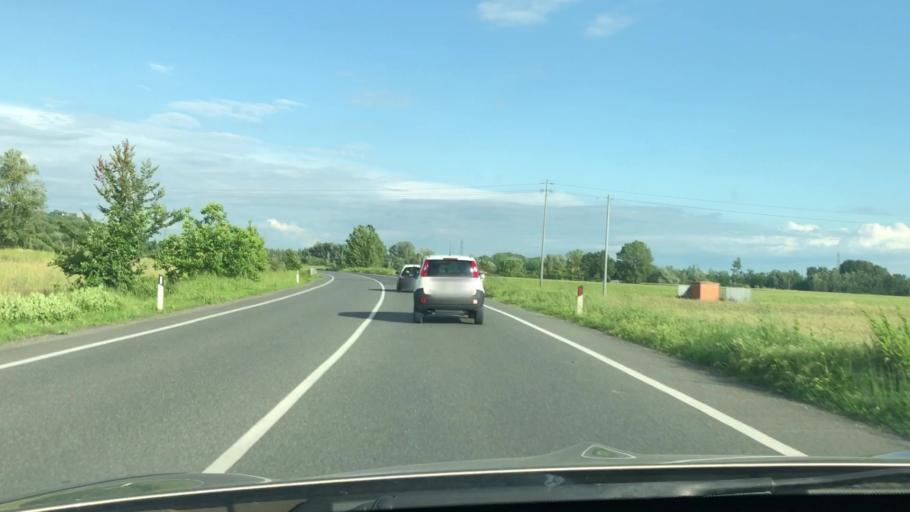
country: IT
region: Tuscany
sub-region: Province of Pisa
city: Treggiaia
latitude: 43.6203
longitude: 10.6664
